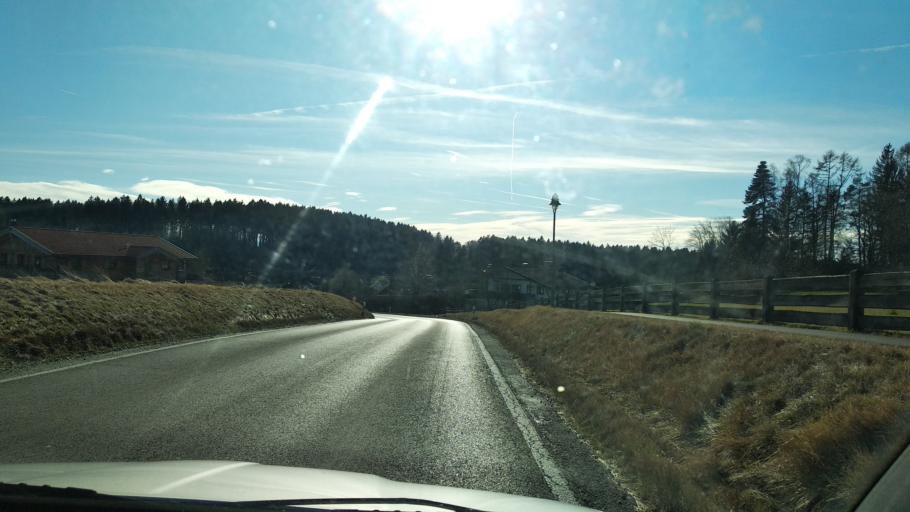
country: DE
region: Bavaria
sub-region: Upper Bavaria
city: Oberpframmern
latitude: 48.0178
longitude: 11.8100
